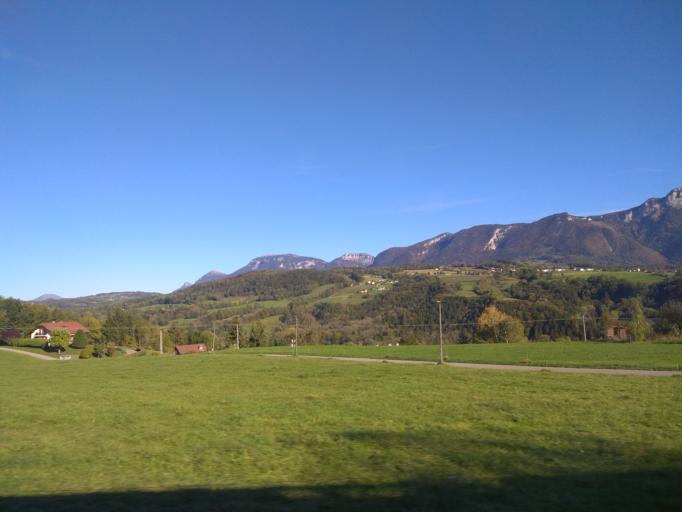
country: FR
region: Rhone-Alpes
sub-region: Departement de la Haute-Savoie
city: Saint-Martin-Bellevue
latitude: 45.9836
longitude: 6.1571
